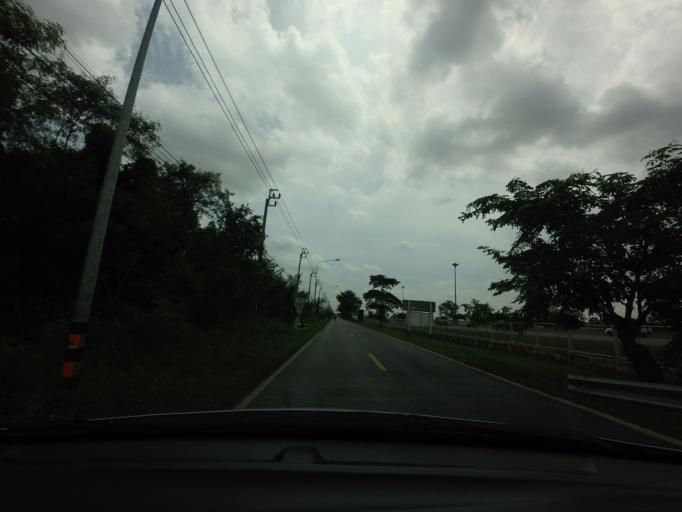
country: TH
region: Bangkok
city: Khan Na Yao
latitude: 13.8807
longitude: 100.6850
